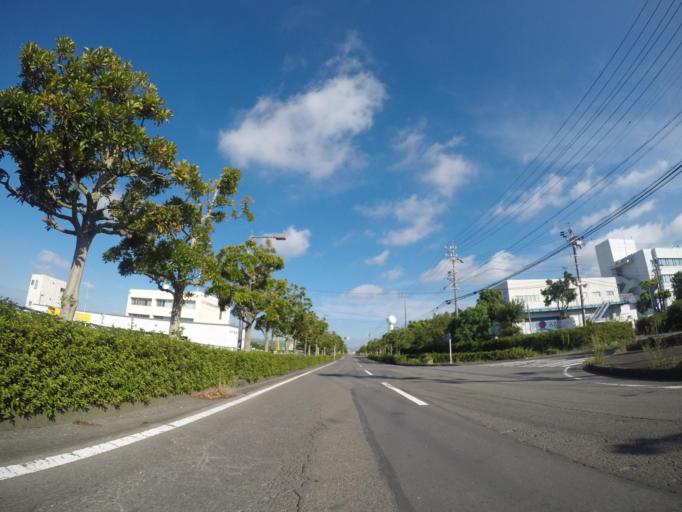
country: JP
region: Shizuoka
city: Fujieda
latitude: 34.7835
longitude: 138.2957
